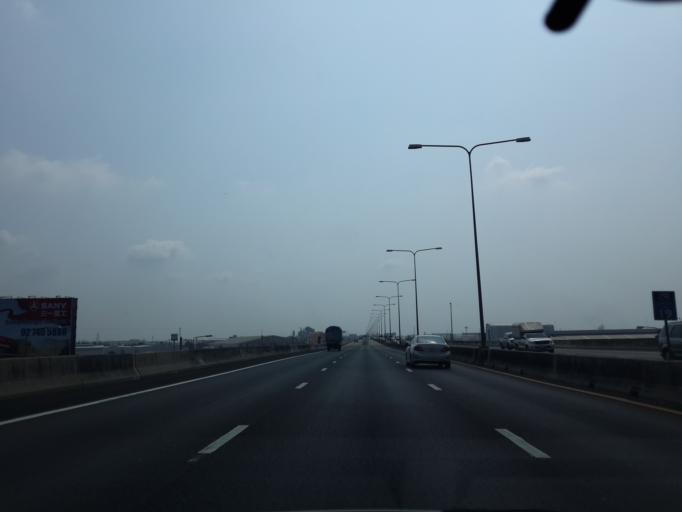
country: TH
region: Samut Prakan
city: Bang Bo District
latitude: 13.6082
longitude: 100.7678
